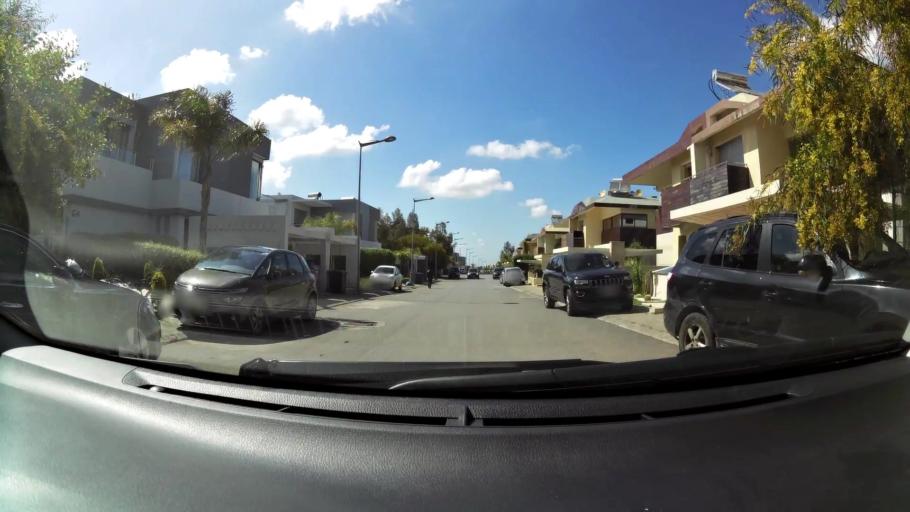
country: MA
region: Grand Casablanca
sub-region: Nouaceur
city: Bouskoura
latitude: 33.4647
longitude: -7.6023
